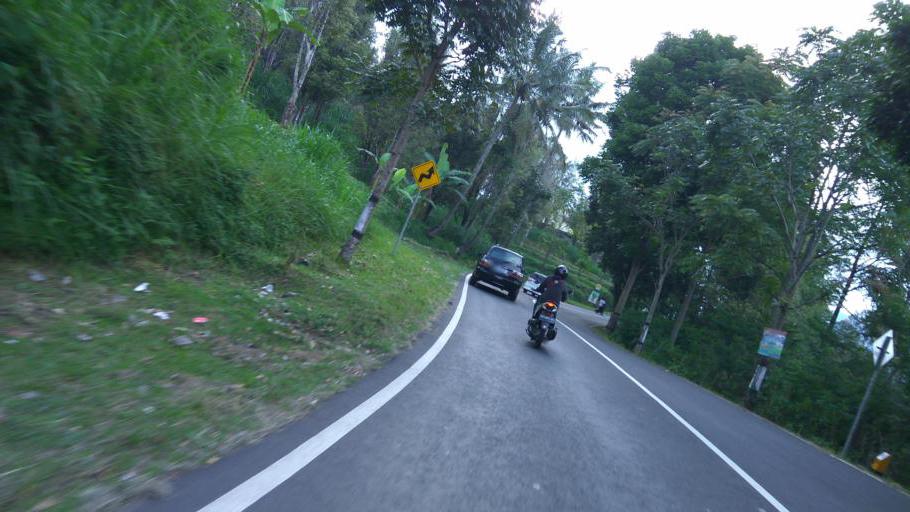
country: ID
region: Central Java
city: Gunung Kendil
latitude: -7.3730
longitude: 110.4445
